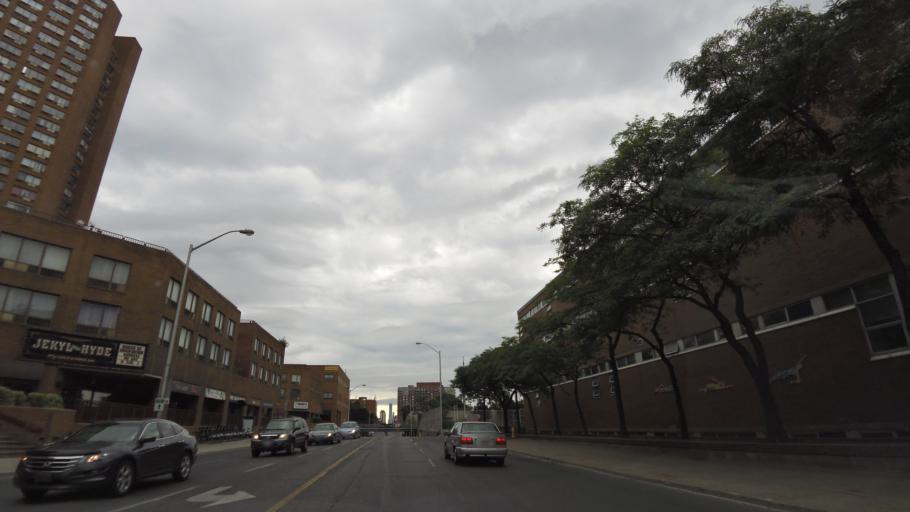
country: CA
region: Ontario
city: Toronto
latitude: 43.6564
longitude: -79.4520
